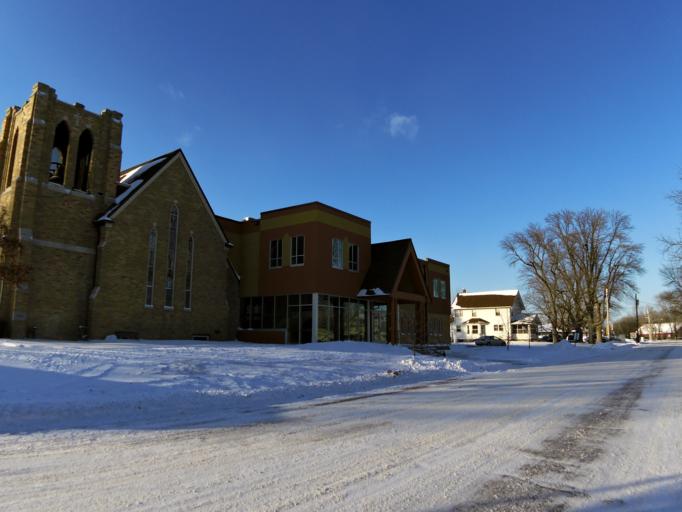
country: US
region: Minnesota
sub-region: Washington County
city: Lake Elmo
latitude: 45.0011
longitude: -92.8787
